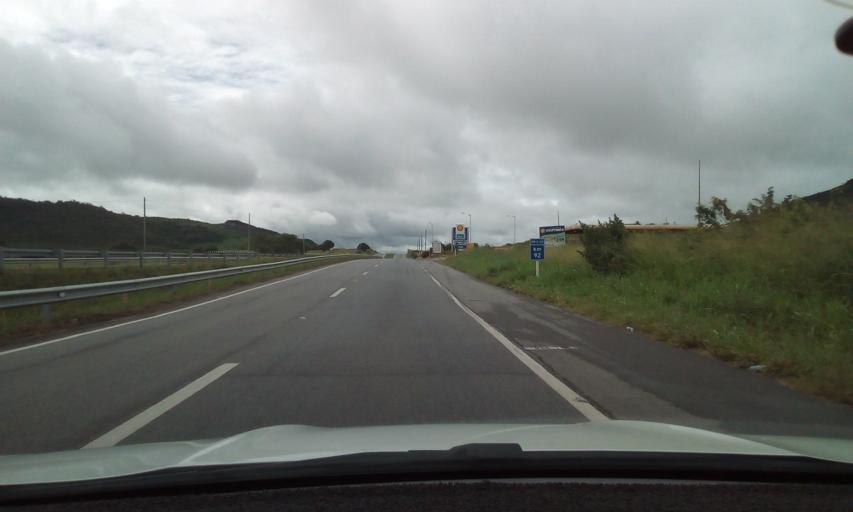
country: BR
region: Paraiba
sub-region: Gurinhem
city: Gurinhem
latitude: -7.1787
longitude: -35.4215
